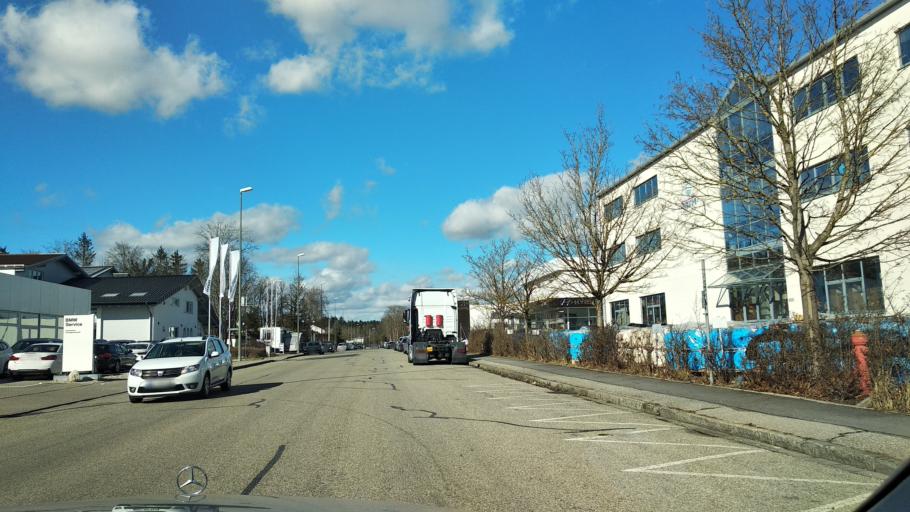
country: DE
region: Bavaria
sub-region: Upper Bavaria
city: Waldkraiburg
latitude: 48.2133
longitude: 12.4119
